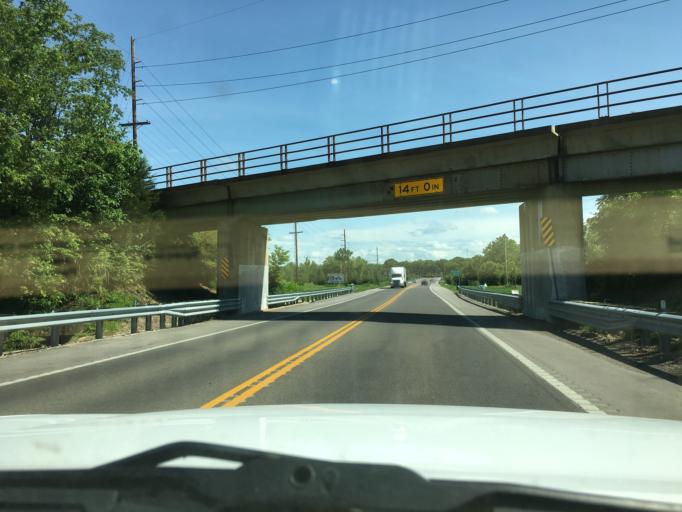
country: US
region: Missouri
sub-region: Franklin County
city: Union
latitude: 38.4511
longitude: -91.0006
